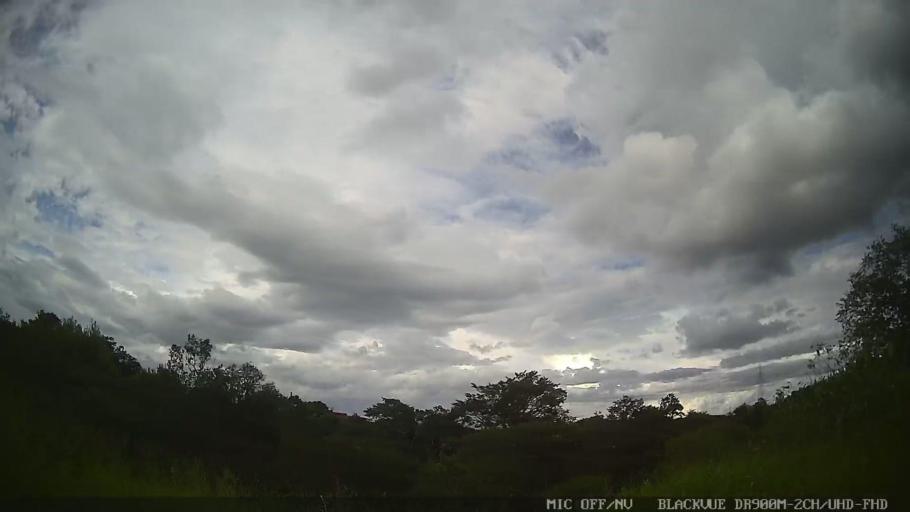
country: BR
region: Sao Paulo
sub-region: Mogi das Cruzes
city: Mogi das Cruzes
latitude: -23.5321
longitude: -46.1589
